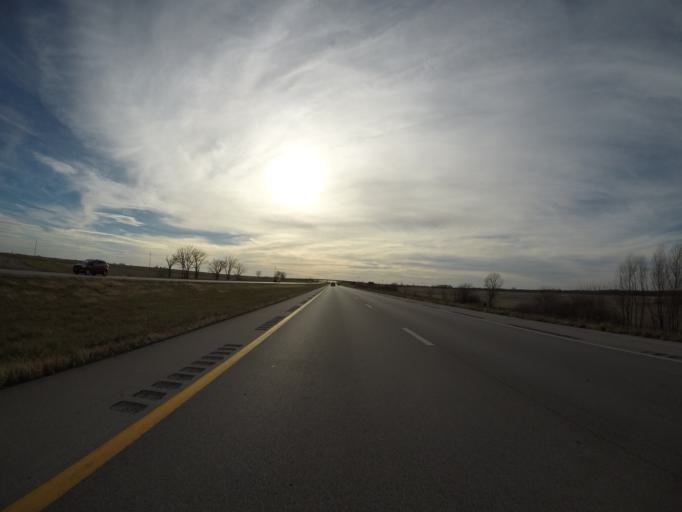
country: US
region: Kansas
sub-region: Johnson County
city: Edgerton
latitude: 38.7406
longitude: -95.0143
